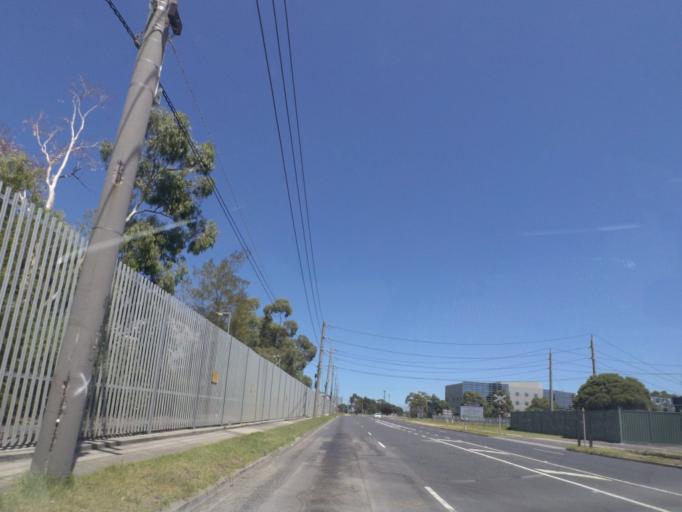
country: AU
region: Victoria
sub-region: Maribyrnong
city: Yarraville
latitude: -37.8243
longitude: 144.9115
